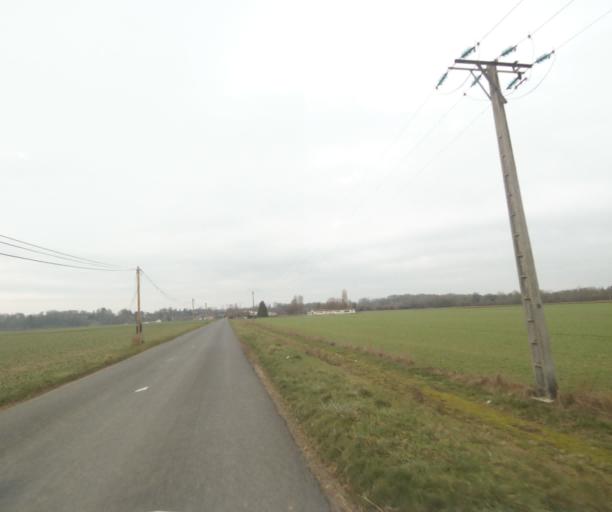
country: FR
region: Champagne-Ardenne
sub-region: Departement de la Haute-Marne
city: Villiers-en-Lieu
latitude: 48.6386
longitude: 4.8665
